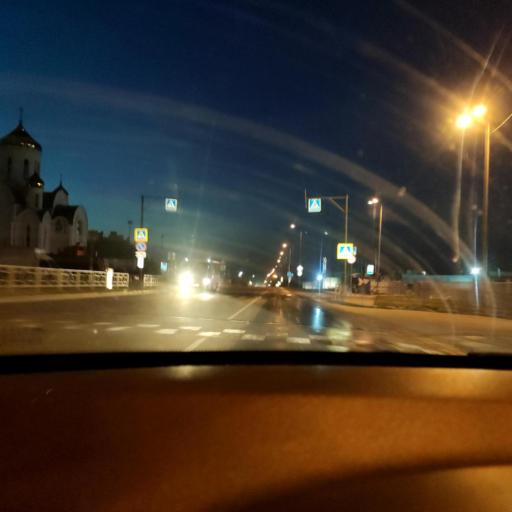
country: RU
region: Samara
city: Petra-Dubrava
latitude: 53.3170
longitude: 50.3035
